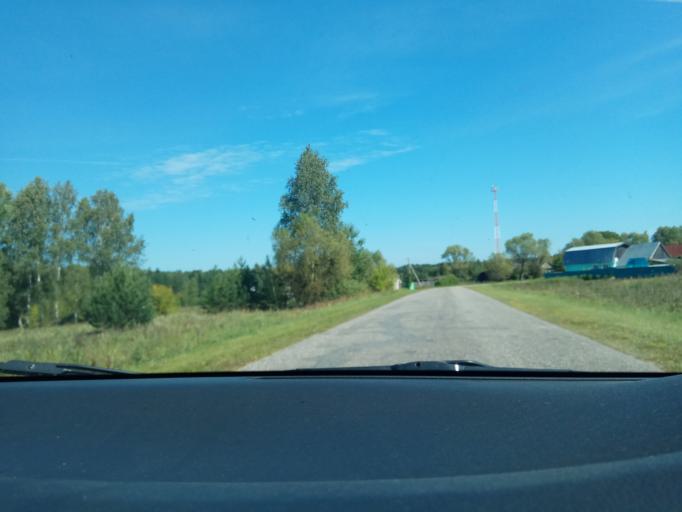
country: RU
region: Vladimir
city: Dobryatino
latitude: 55.7331
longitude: 41.4311
